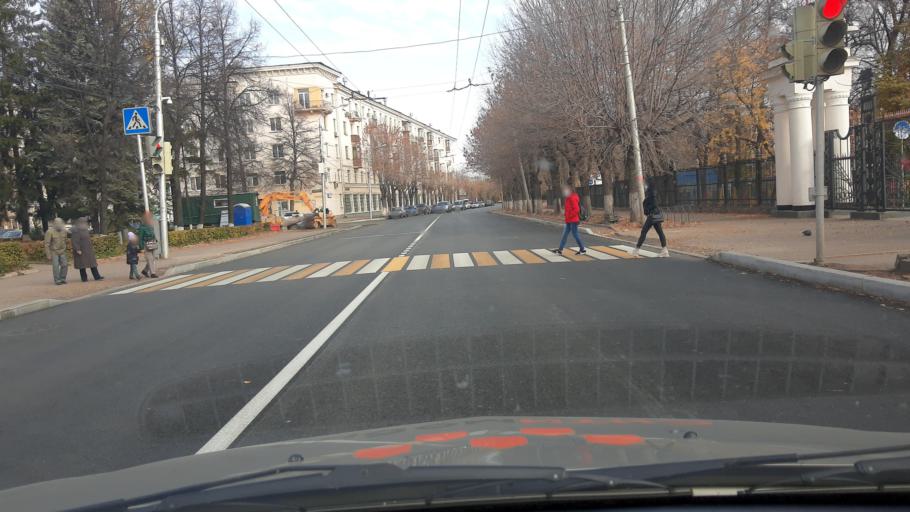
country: RU
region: Bashkortostan
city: Ufa
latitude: 54.7399
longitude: 55.9477
